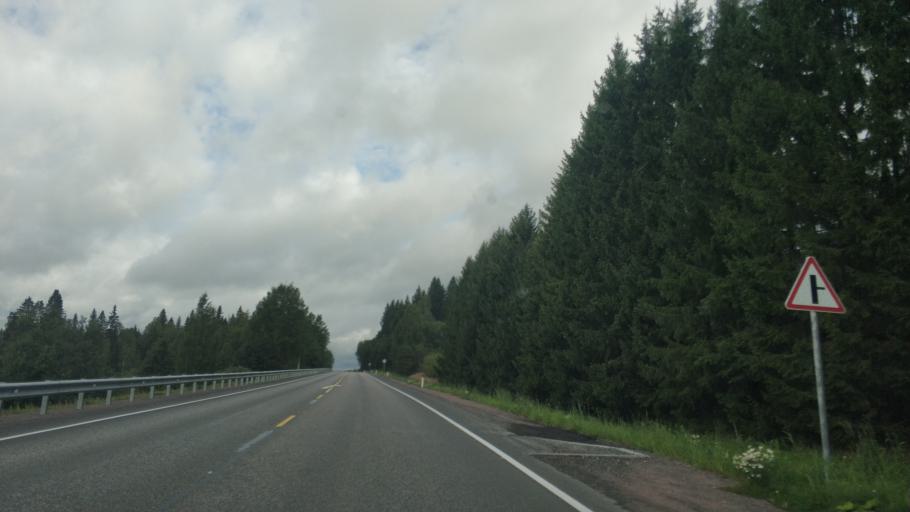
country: RU
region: Republic of Karelia
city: Khelyulya
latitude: 61.7923
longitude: 30.6287
